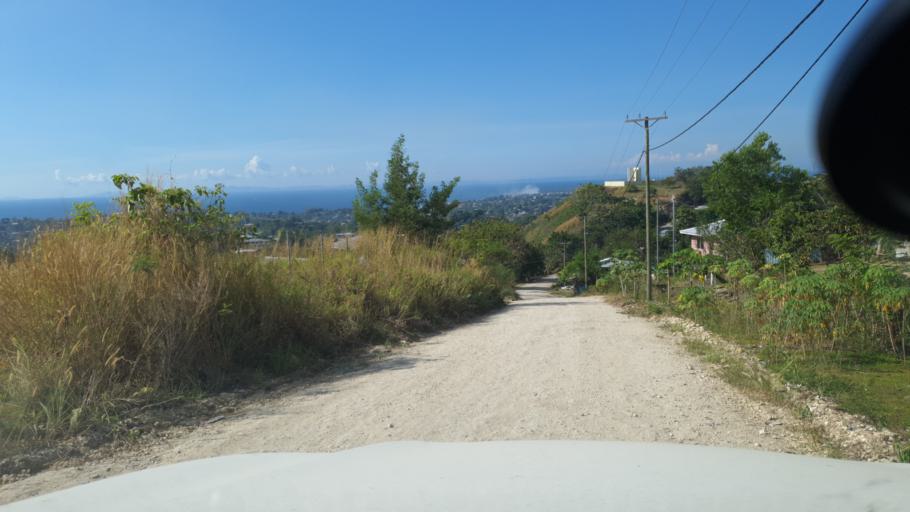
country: SB
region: Guadalcanal
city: Honiara
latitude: -9.4574
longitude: 159.9775
